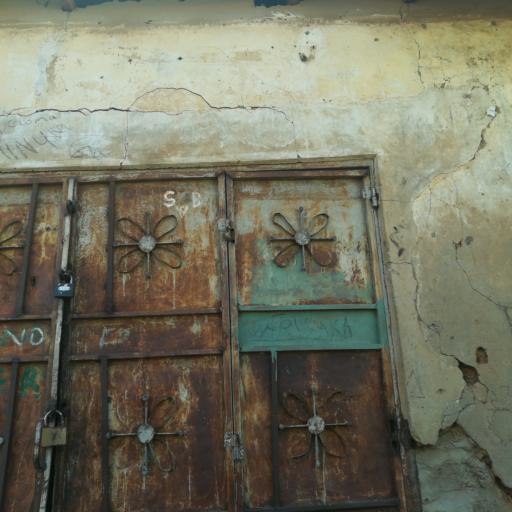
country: NG
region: Kano
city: Kano
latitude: 12.0157
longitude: 8.5154
